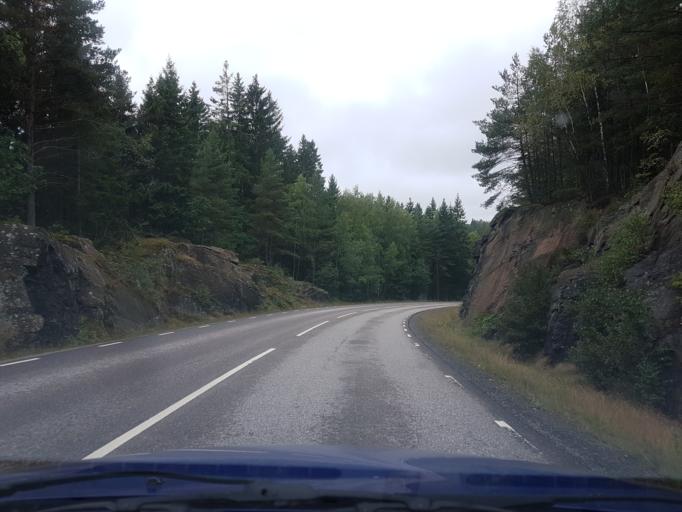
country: SE
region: Vaestra Goetaland
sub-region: Ale Kommun
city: Skepplanda
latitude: 57.9469
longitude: 12.2044
